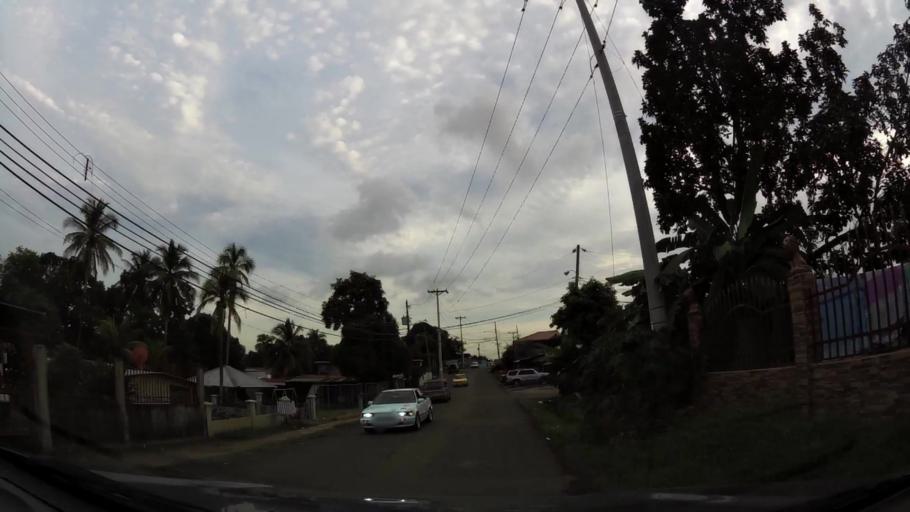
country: PA
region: Panama
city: Tocumen
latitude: 9.0864
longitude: -79.3938
